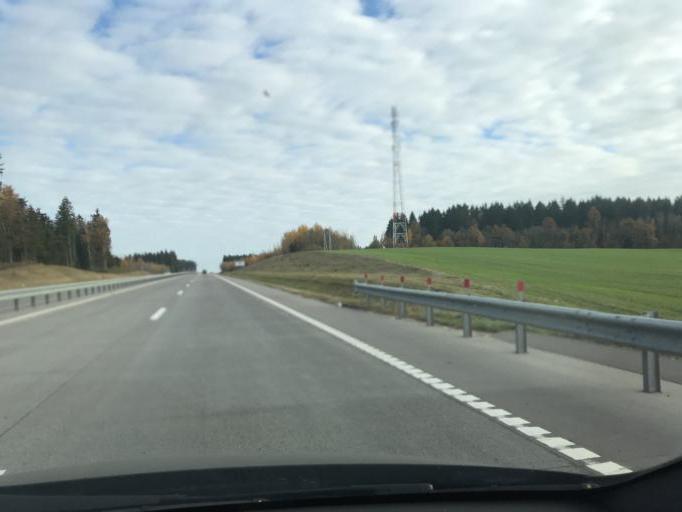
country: BY
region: Minsk
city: Pyatryshki
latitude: 54.0645
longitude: 27.2428
